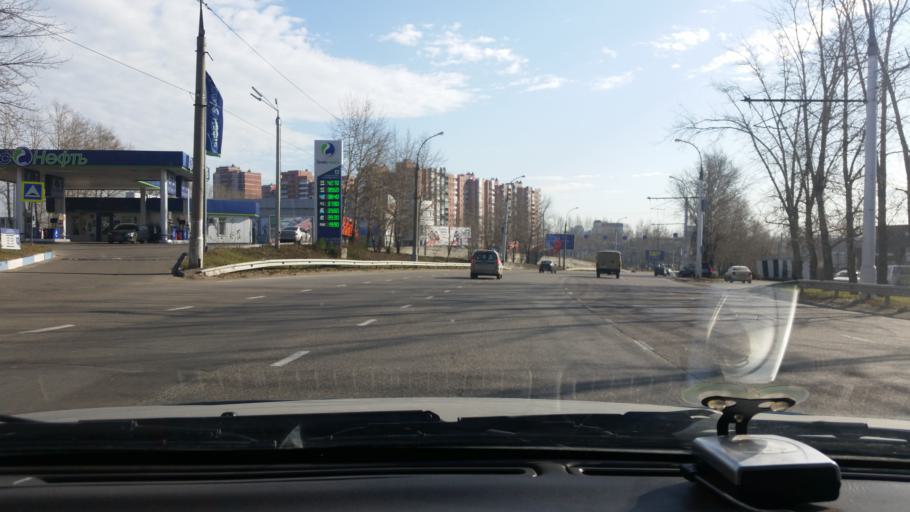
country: RU
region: Irkutsk
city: Dzerzhinsk
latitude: 52.2630
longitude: 104.3500
